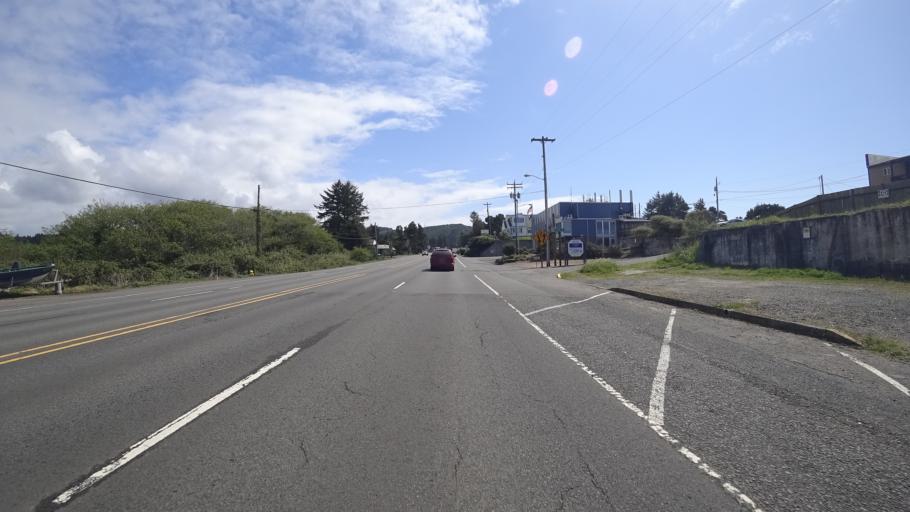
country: US
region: Oregon
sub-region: Lincoln County
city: Depoe Bay
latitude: 44.8084
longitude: -124.0617
